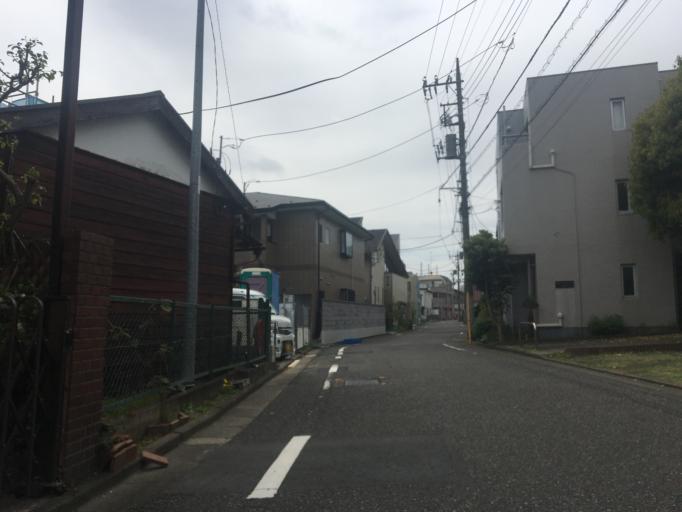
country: JP
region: Tokyo
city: Tokyo
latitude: 35.6789
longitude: 139.6506
